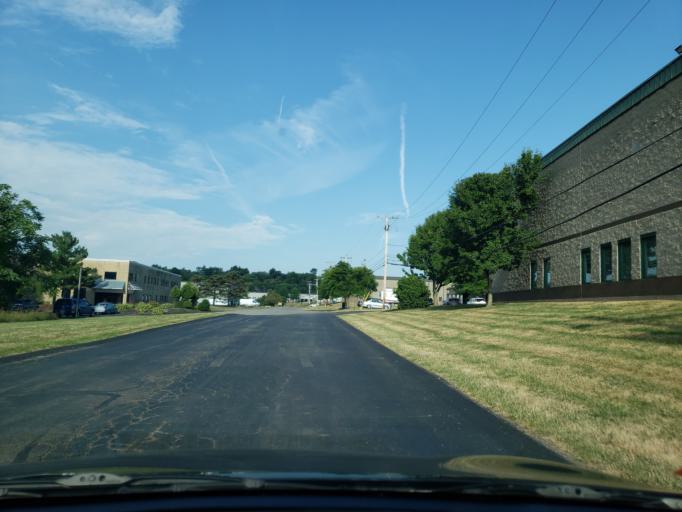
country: US
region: Pennsylvania
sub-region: Allegheny County
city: Coraopolis
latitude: 40.5298
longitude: -80.1333
